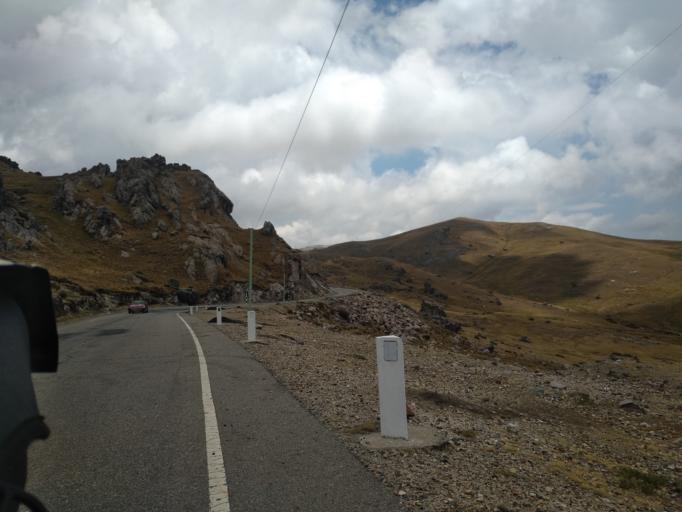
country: PE
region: La Libertad
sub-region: Provincia de Santiago de Chuco
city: Quiruvilca
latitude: -7.9738
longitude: -78.2154
